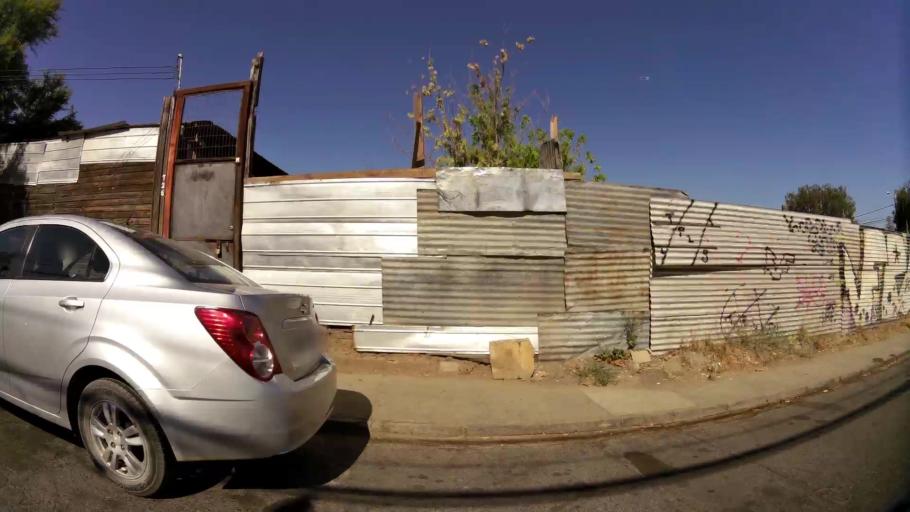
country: CL
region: Maule
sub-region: Provincia de Talca
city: Talca
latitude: -35.4311
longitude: -71.6671
